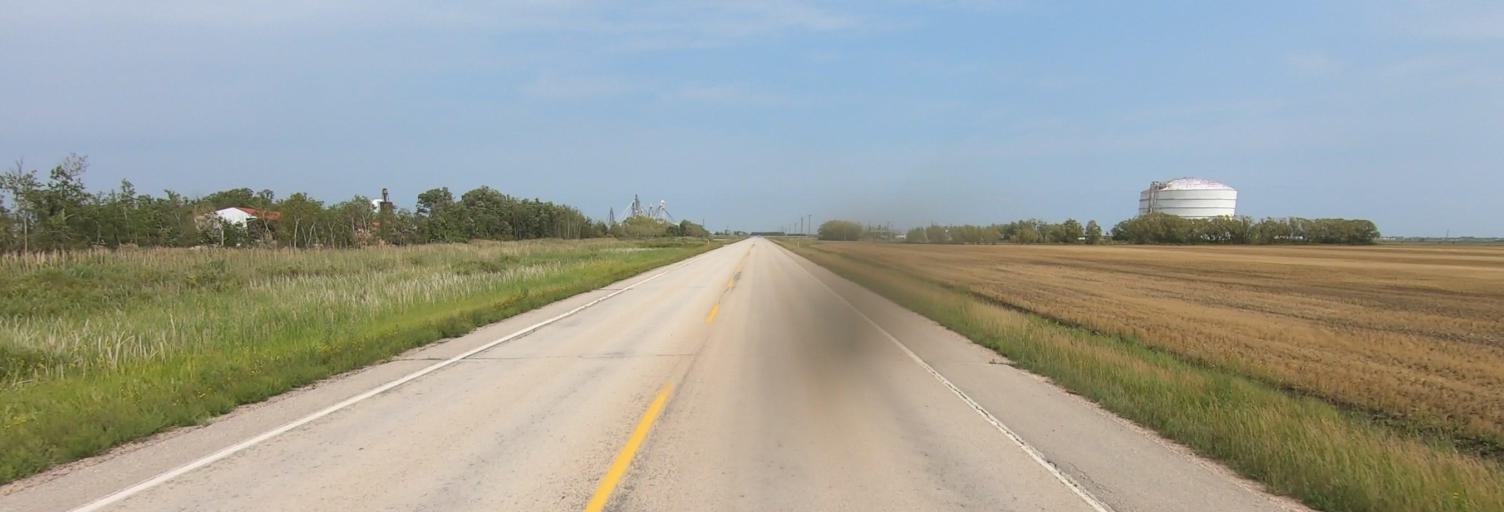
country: CA
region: Manitoba
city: Winnipeg
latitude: 49.7580
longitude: -97.2418
